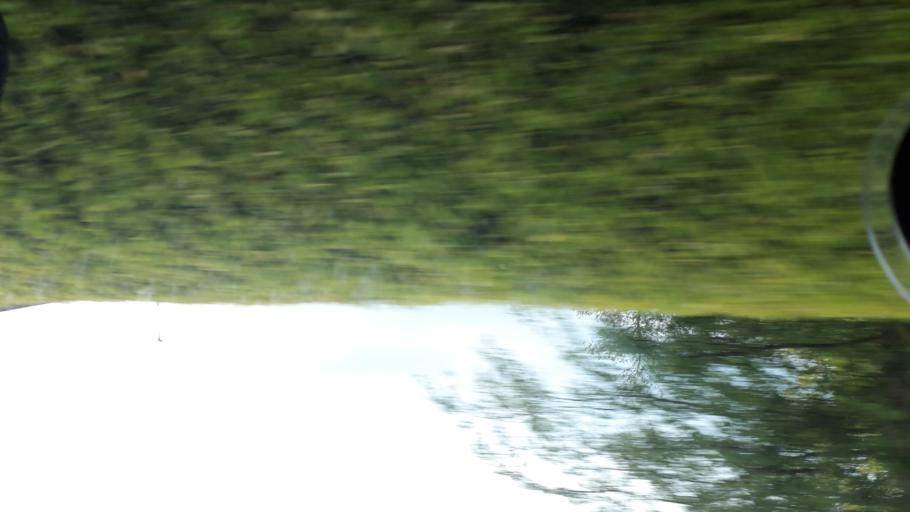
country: IE
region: Leinster
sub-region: Kildare
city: Celbridge
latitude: 53.3251
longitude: -6.5494
